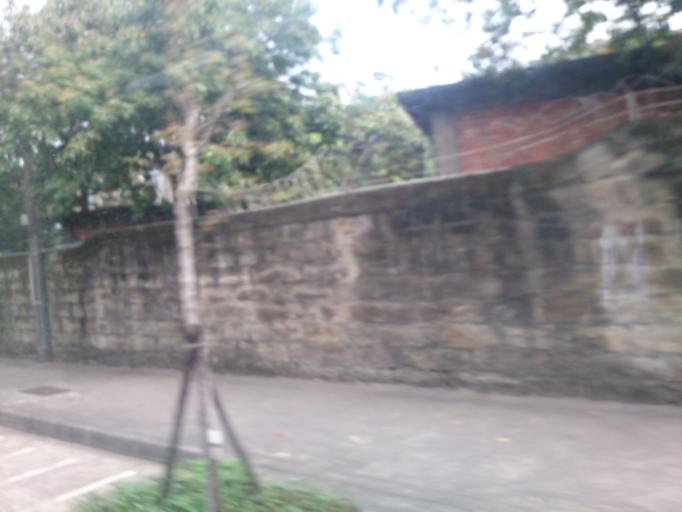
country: TW
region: Taipei
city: Taipei
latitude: 25.0881
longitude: 121.5273
